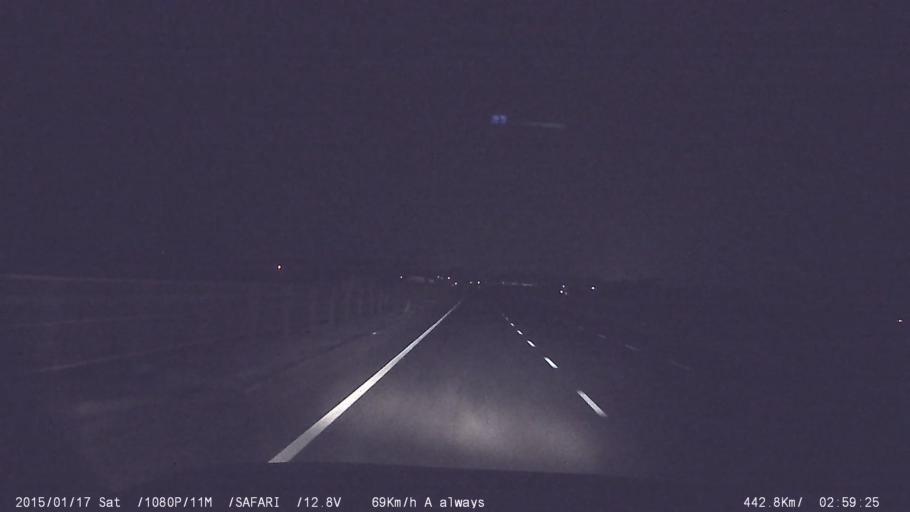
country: IN
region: Tamil Nadu
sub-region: Krishnagiri
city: Hosur
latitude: 12.7737
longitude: 77.7825
